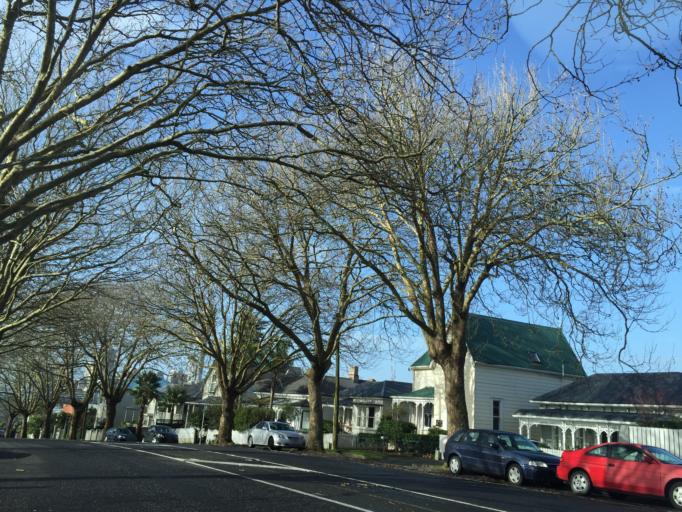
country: NZ
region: Auckland
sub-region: Auckland
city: Auckland
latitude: -36.8524
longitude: 174.7476
